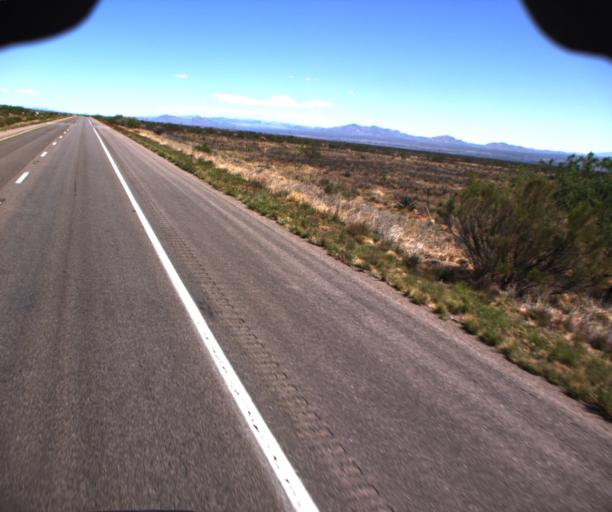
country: US
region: Arizona
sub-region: Cochise County
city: Whetstone
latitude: 31.8204
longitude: -110.3465
